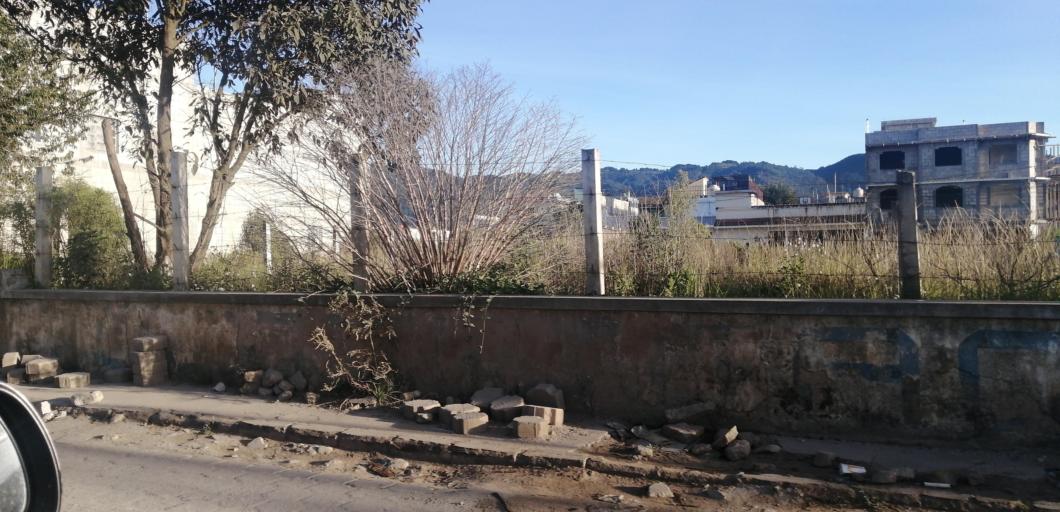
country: GT
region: Quetzaltenango
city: Olintepeque
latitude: 14.8671
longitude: -91.5255
